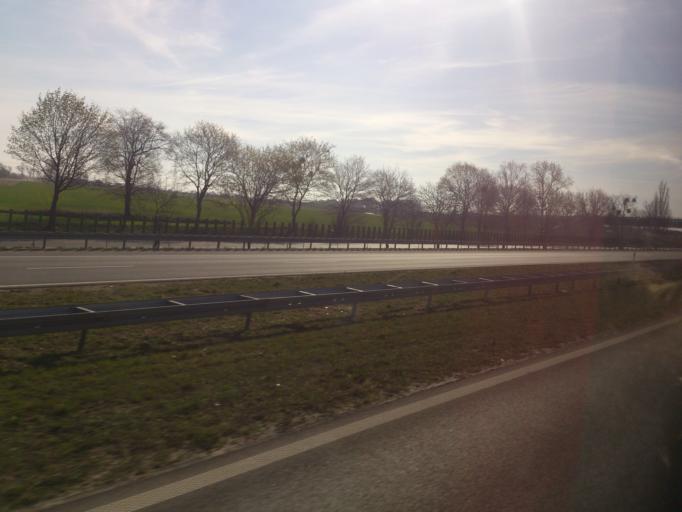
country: PL
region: Kujawsko-Pomorskie
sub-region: Powiat aleksandrowski
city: Raciazek
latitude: 52.8473
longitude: 18.7849
